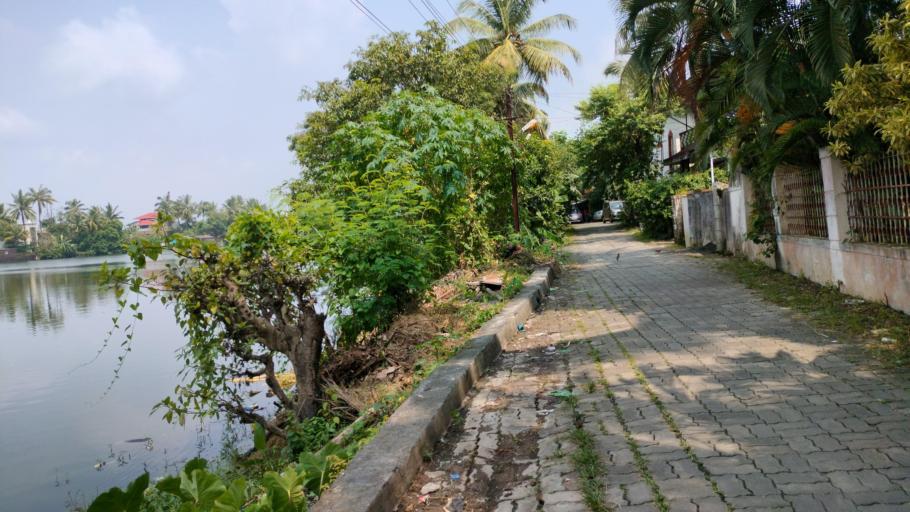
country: IN
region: Maharashtra
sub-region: Thane
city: Virar
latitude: 19.3990
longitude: 72.7809
